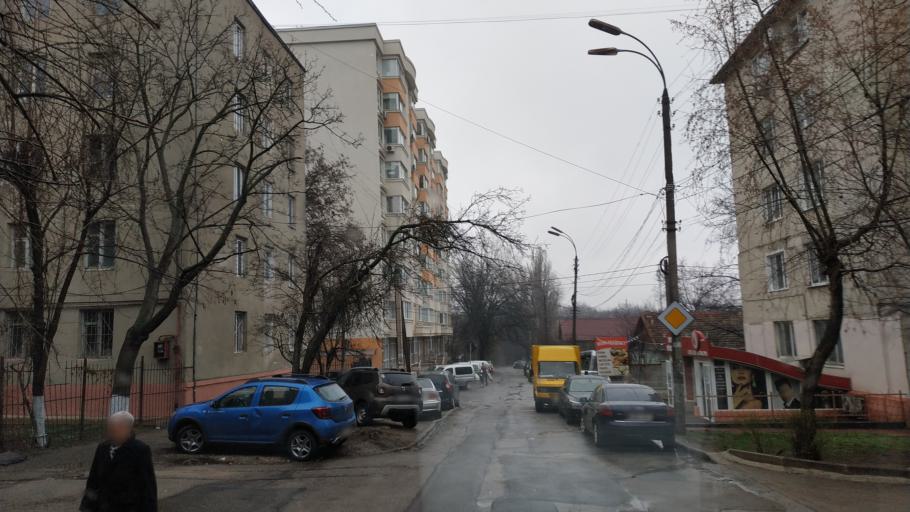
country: MD
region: Chisinau
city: Vatra
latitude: 47.0358
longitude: 28.7813
